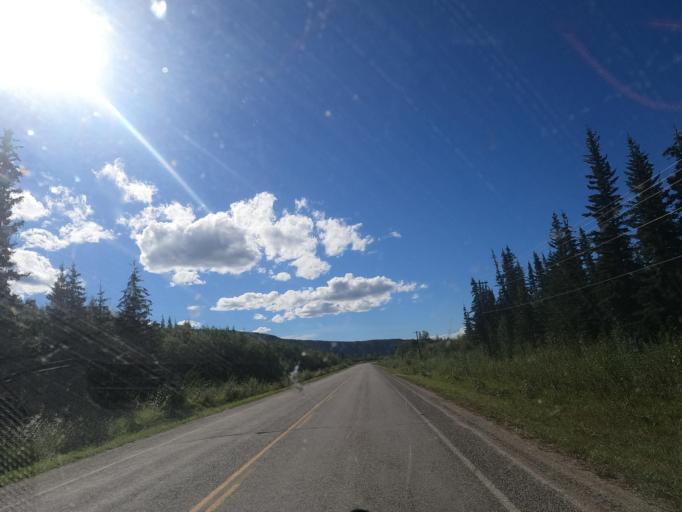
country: CA
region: Yukon
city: Dawson City
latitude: 64.0310
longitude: -139.1721
